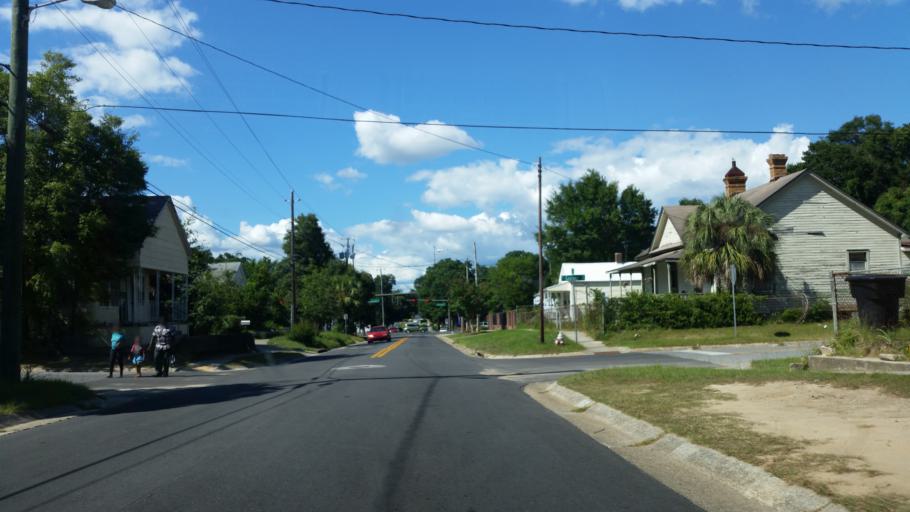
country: US
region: Florida
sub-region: Escambia County
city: Pensacola
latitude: 30.4190
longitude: -87.2301
